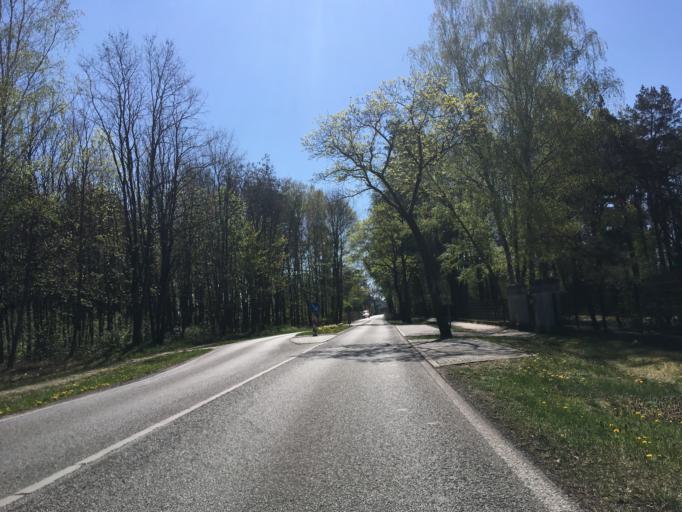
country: DE
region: Brandenburg
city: Bernau bei Berlin
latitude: 52.7088
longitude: 13.5839
